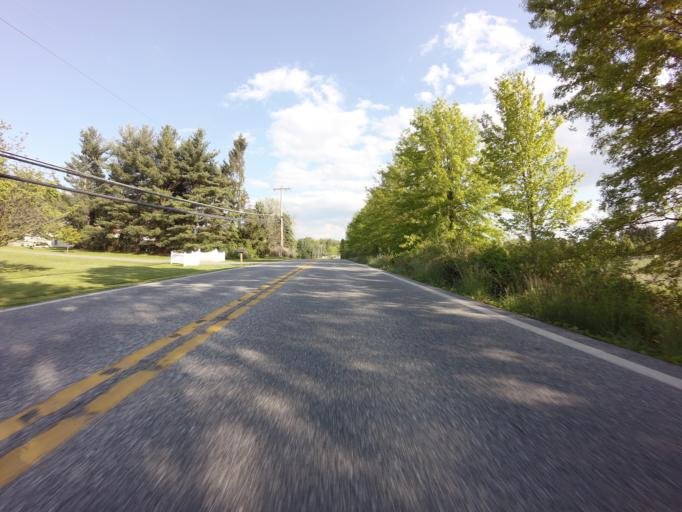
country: US
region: Maryland
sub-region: Baltimore County
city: Cockeysville
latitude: 39.4762
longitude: -76.7072
